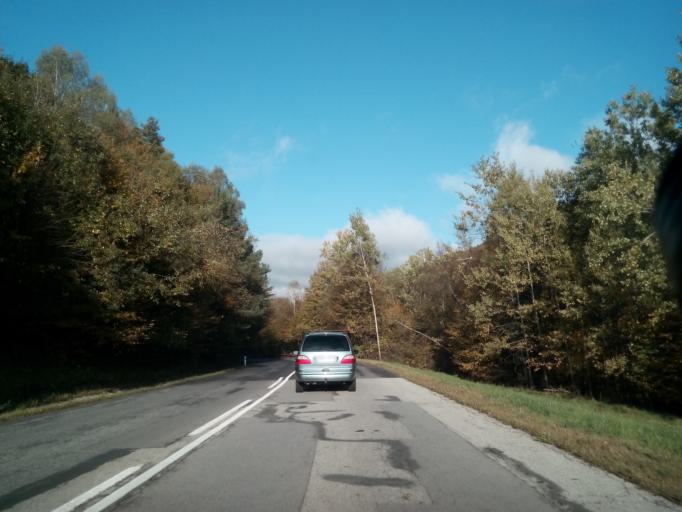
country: SK
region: Kosicky
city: Gelnica
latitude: 48.9045
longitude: 20.9839
